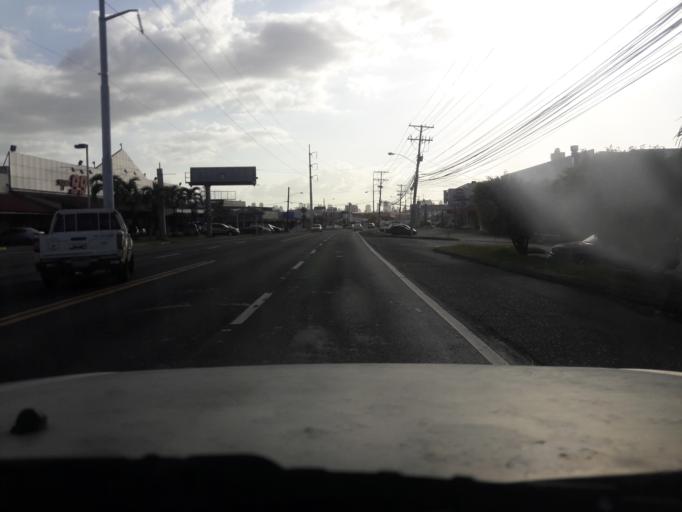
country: PA
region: Panama
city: San Miguelito
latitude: 9.0309
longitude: -79.4759
